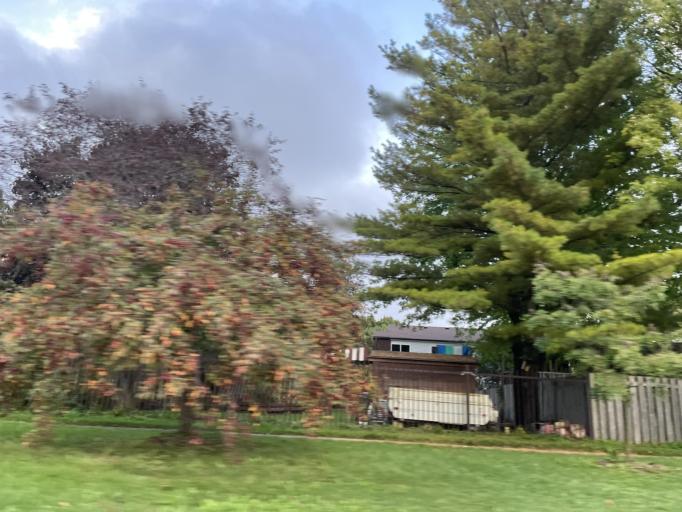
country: CA
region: Ontario
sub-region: Wellington County
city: Guelph
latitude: 43.5161
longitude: -80.2786
